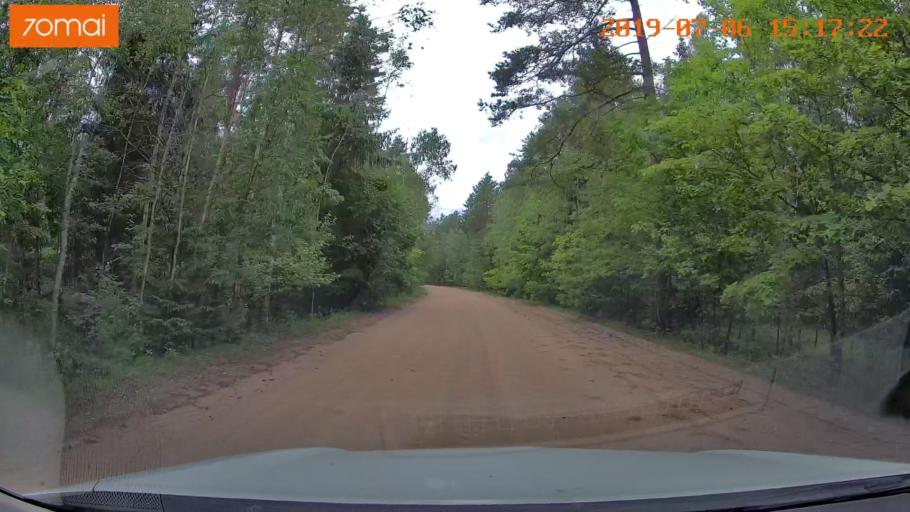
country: BY
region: Minsk
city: Ivyanyets
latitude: 53.9877
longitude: 26.6670
